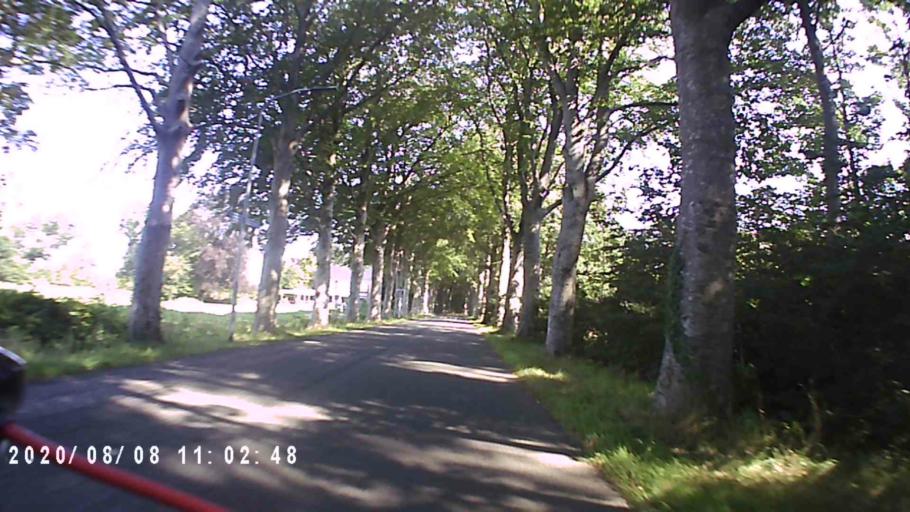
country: NL
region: Groningen
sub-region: Gemeente Leek
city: Leek
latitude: 53.1564
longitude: 6.3953
